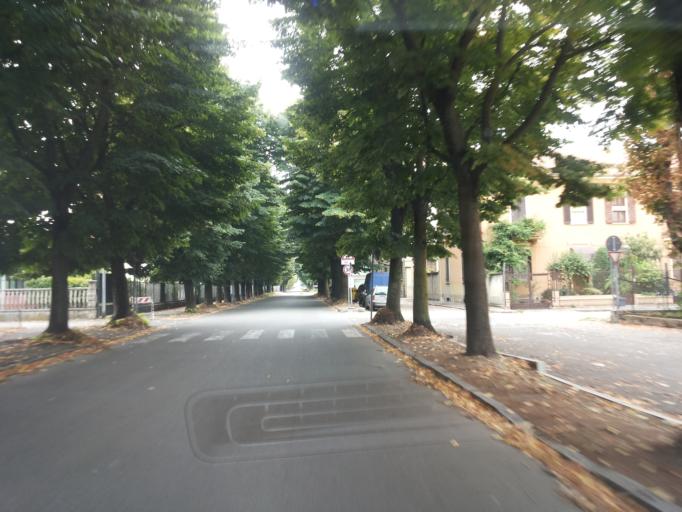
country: IT
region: Piedmont
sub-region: Provincia di Vercelli
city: Vercelli
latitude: 45.3295
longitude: 8.4343
